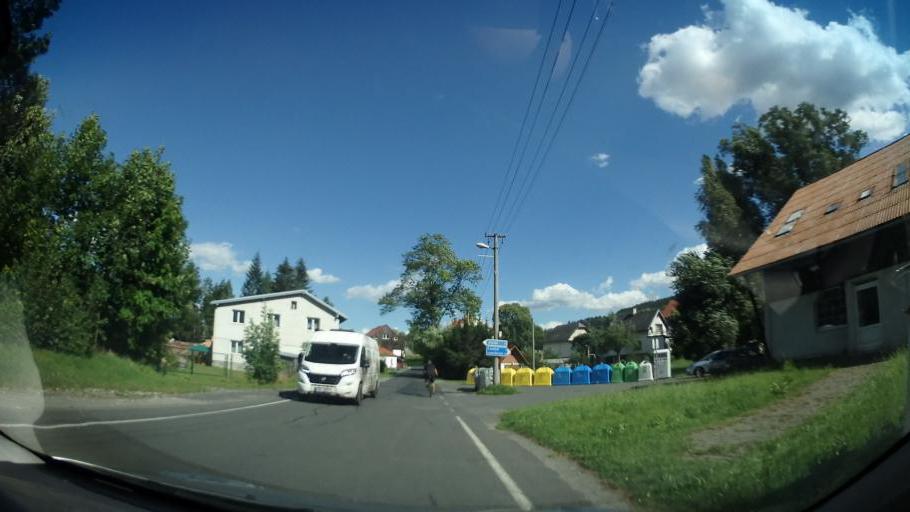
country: CZ
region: Olomoucky
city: Vapenna
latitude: 50.2226
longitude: 17.1054
